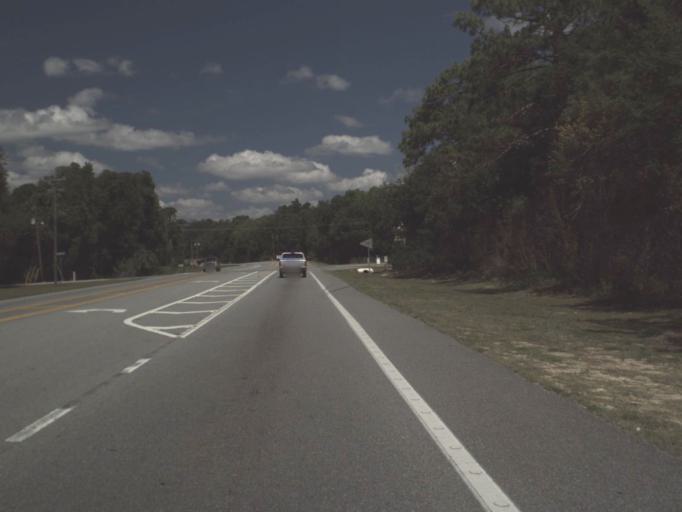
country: US
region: Florida
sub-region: Marion County
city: Silver Springs Shores
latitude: 29.1748
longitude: -81.8705
